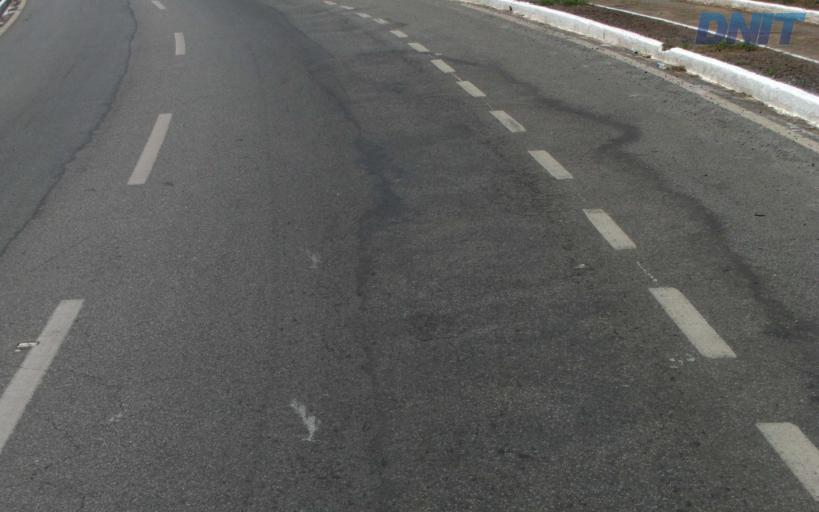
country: BR
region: Minas Gerais
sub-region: Coronel Fabriciano
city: Coronel Fabriciano
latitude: -19.5057
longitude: -42.5931
